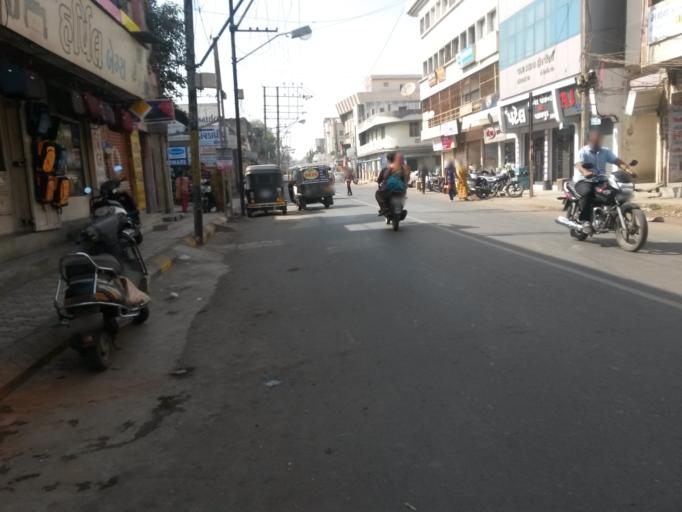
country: IN
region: Gujarat
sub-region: Rajkot
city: Rajkot
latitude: 22.2889
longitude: 70.8059
